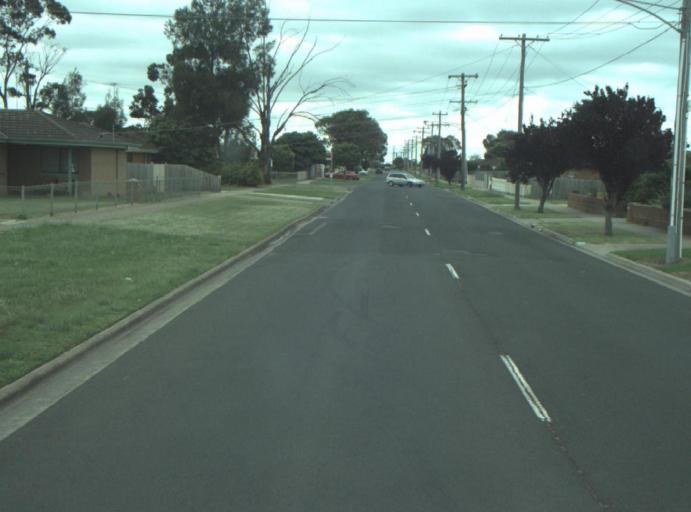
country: AU
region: Victoria
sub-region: Greater Geelong
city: Bell Post Hill
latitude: -38.0762
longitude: 144.3397
